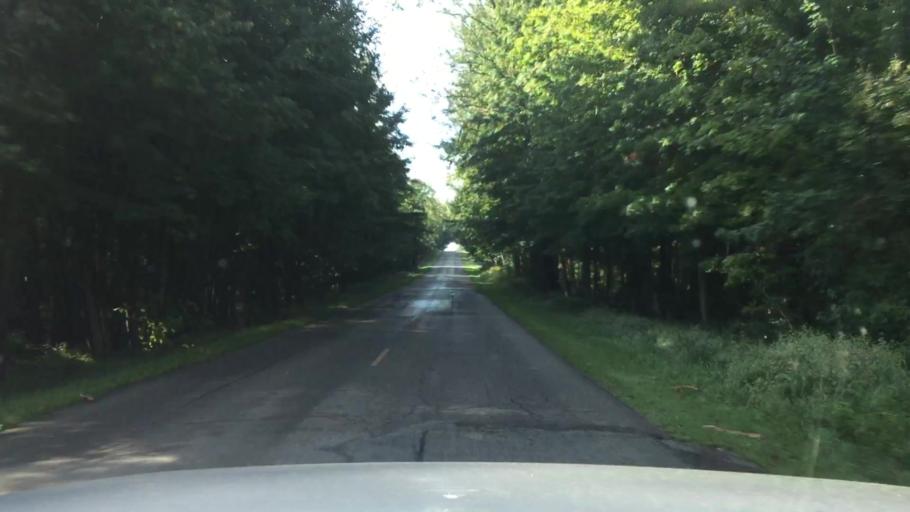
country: US
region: Michigan
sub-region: Lenawee County
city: Hudson
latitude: 41.9246
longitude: -84.4205
